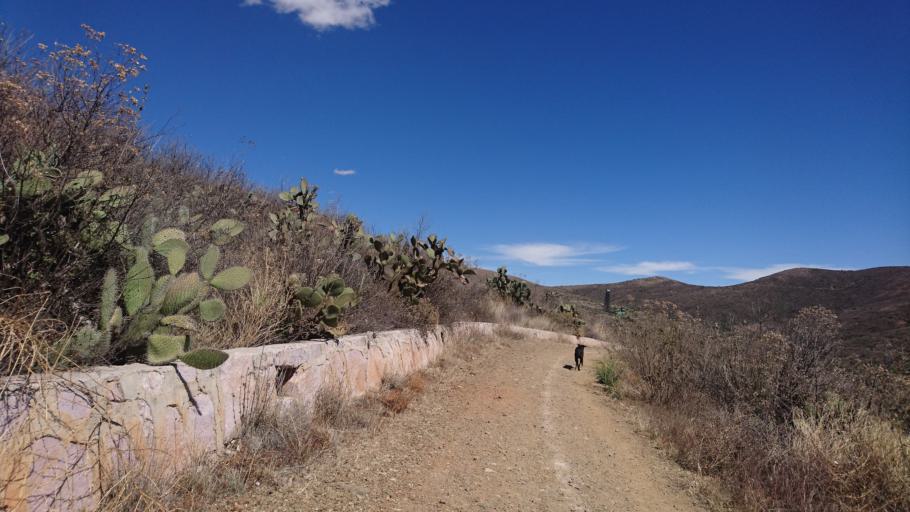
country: MX
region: Zacatecas
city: Zacatecas
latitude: 22.7807
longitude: -102.5468
